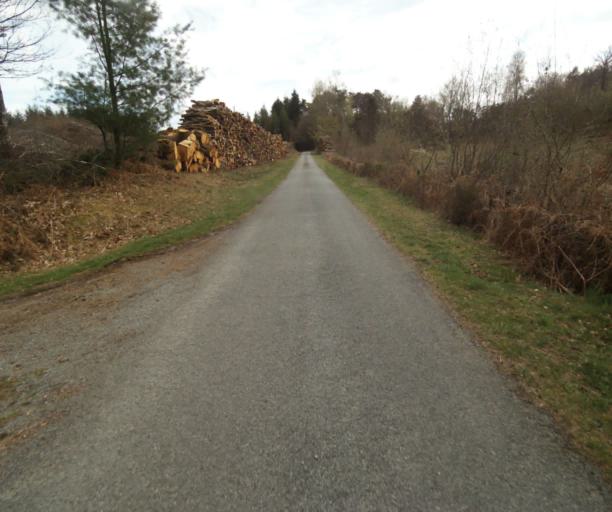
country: FR
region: Limousin
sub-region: Departement de la Correze
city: Argentat
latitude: 45.1941
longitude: 1.9277
